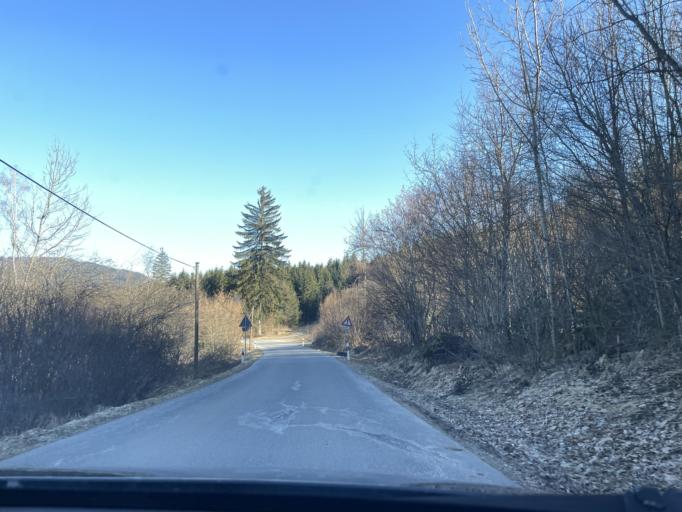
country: DE
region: Bavaria
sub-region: Lower Bavaria
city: Geiersthal
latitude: 49.0749
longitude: 12.9848
